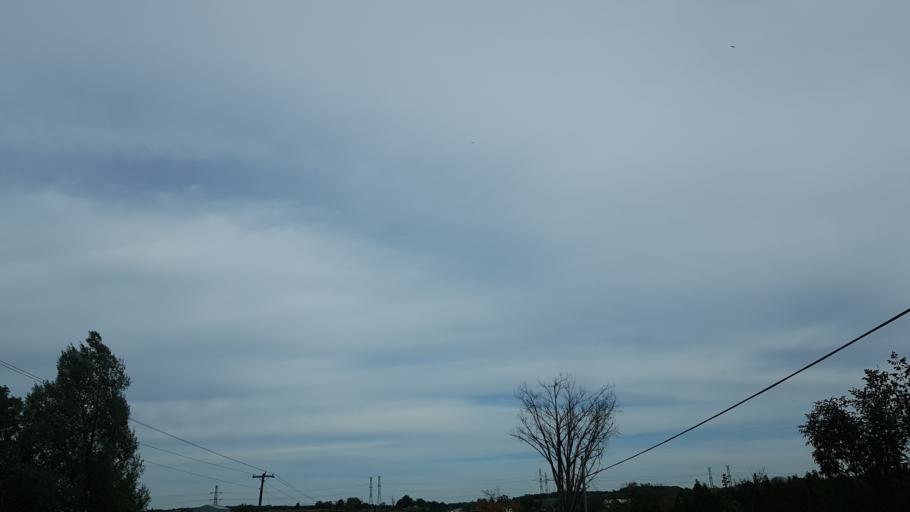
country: CA
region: Ontario
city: Orangeville
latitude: 43.7147
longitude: -80.1159
